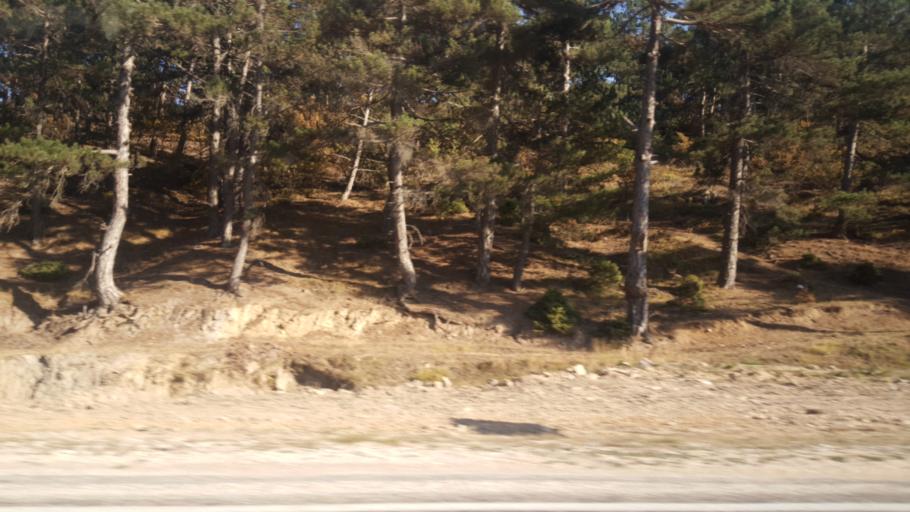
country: TR
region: Eskisehir
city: Kirka
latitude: 39.1100
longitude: 30.5864
